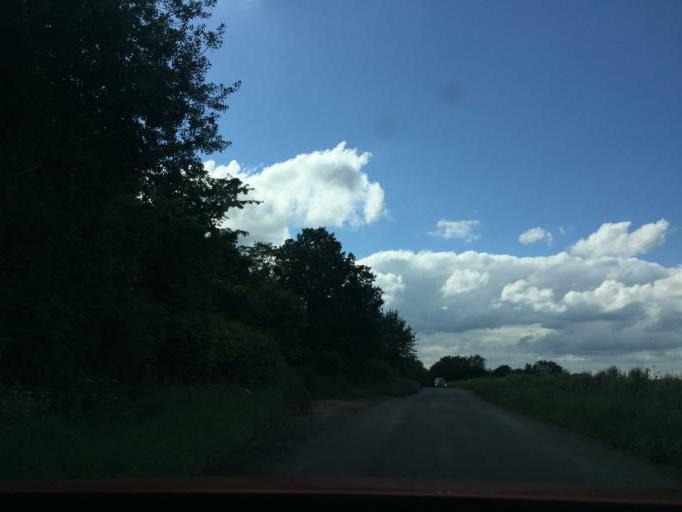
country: GB
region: England
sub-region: Hertfordshire
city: Codicote
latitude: 51.8544
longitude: -0.2479
